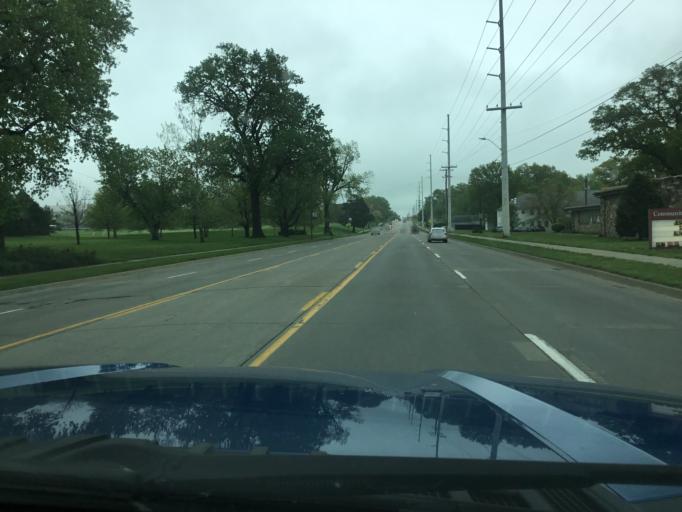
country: US
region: Kansas
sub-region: Shawnee County
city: Topeka
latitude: 39.0297
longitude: -95.7039
